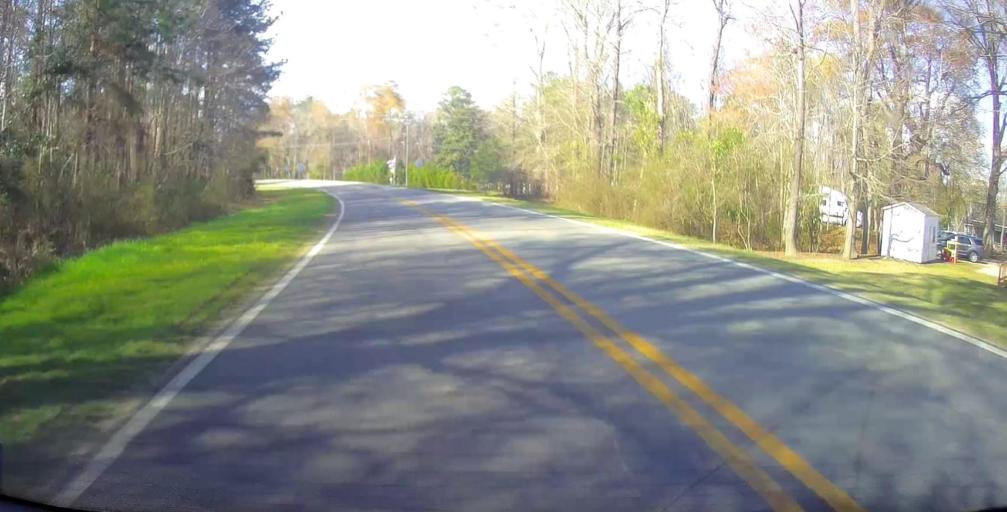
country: US
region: Georgia
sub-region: Laurens County
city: Dublin
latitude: 32.5516
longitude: -82.9929
